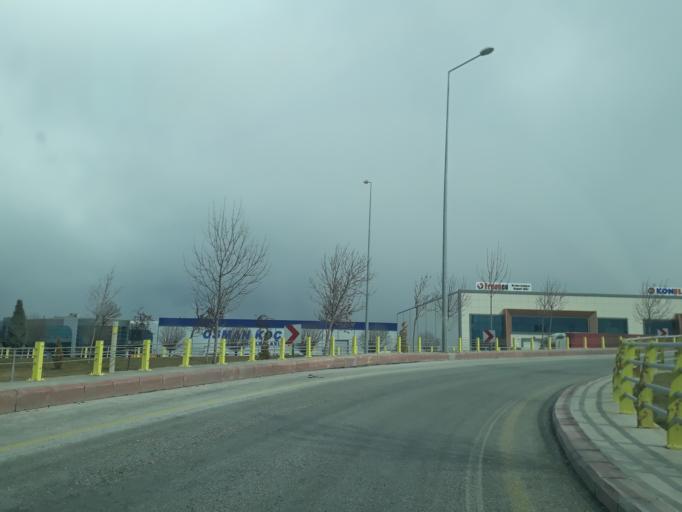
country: TR
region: Konya
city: Asagipinarbasi
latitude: 37.9907
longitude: 32.5961
